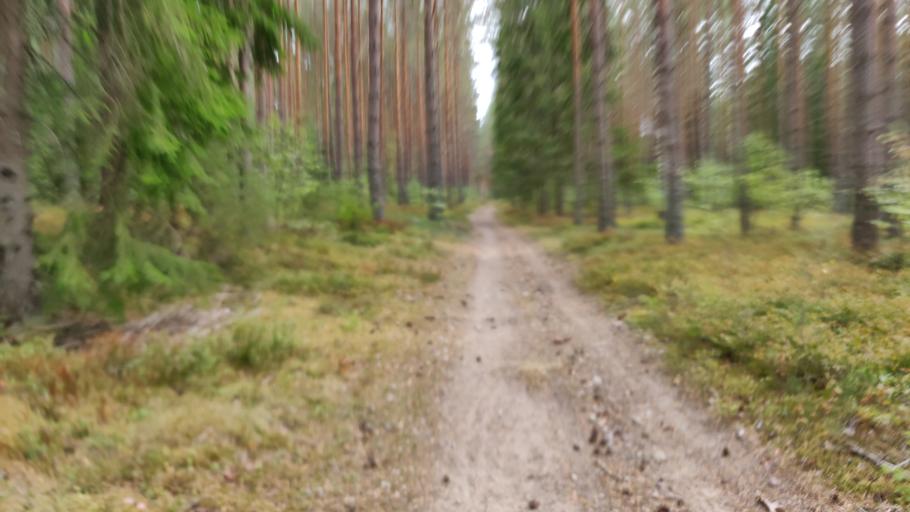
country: SE
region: Vaermland
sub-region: Hagfors Kommun
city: Hagfors
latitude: 60.0386
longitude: 13.5359
